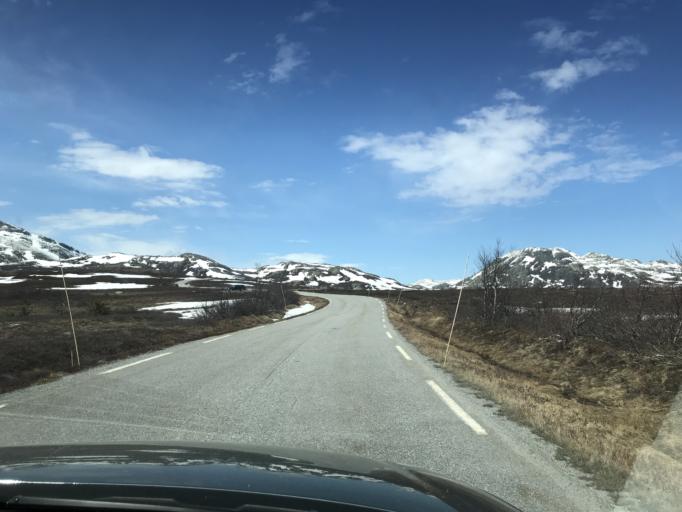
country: NO
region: Telemark
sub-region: Tinn
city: Rjukan
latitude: 59.8032
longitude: 8.7611
